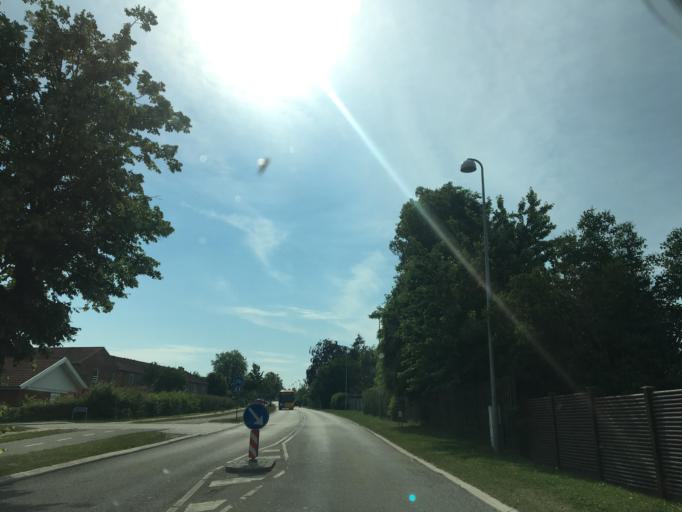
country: DK
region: Zealand
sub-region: Greve Kommune
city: Tune
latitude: 55.5967
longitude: 12.1821
